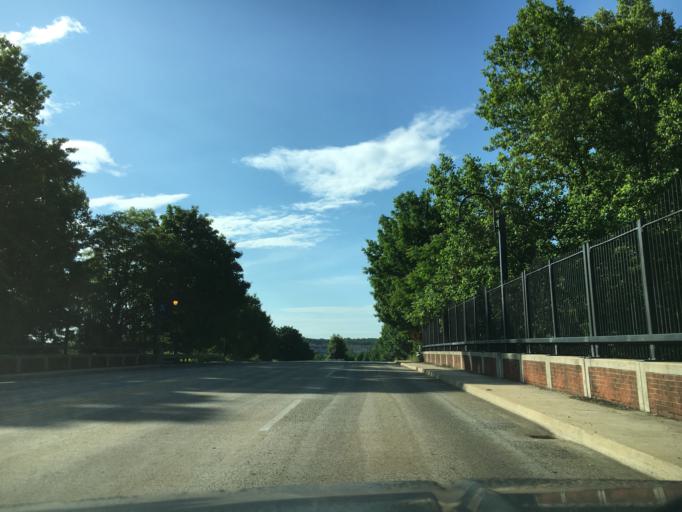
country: US
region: Virginia
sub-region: Bedford County
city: Forest
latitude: 37.3644
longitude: -79.2480
